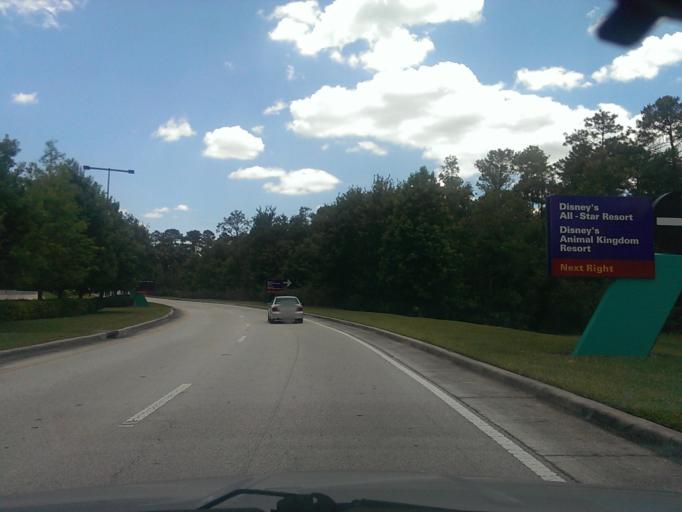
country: US
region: Florida
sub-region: Osceola County
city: Celebration
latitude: 28.3589
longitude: -81.5744
